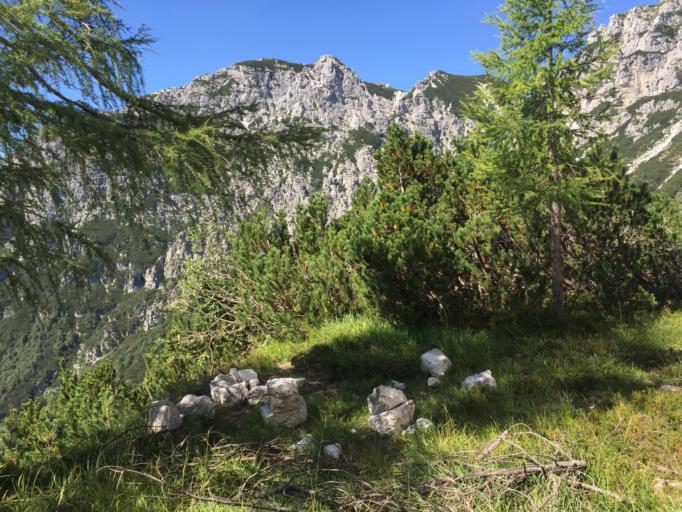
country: IT
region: Friuli Venezia Giulia
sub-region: Provincia di Udine
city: Dogna
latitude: 46.4391
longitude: 13.2674
